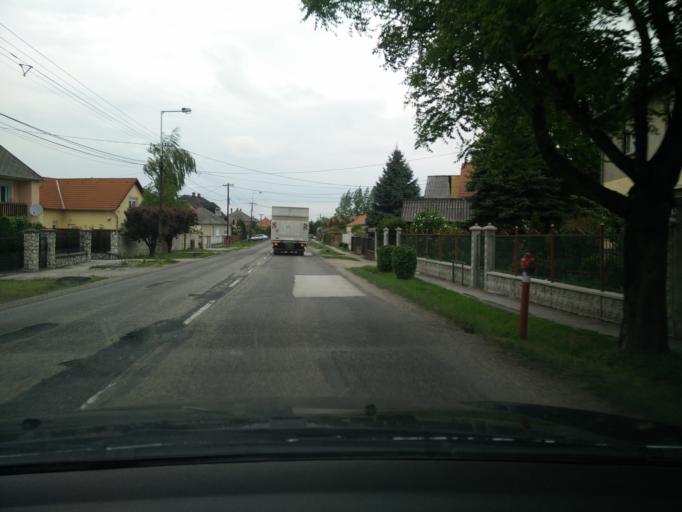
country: HU
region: Gyor-Moson-Sopron
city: Gyorszemere
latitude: 47.5546
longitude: 17.5648
